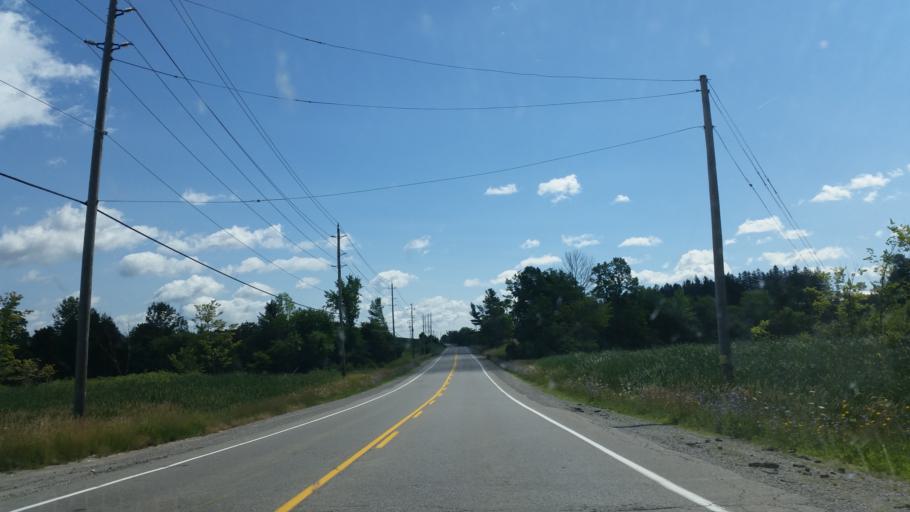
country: CA
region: Ontario
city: Vaughan
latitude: 43.9147
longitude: -79.5909
